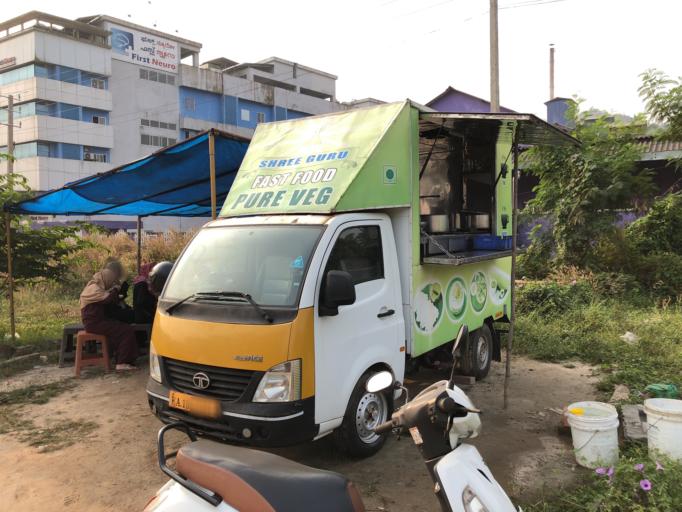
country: IN
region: Karnataka
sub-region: Dakshina Kannada
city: Mangalore
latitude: 12.8710
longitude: 74.8952
